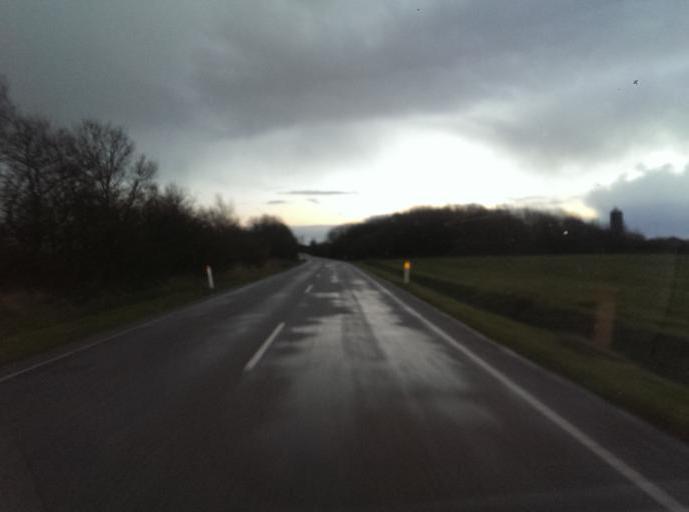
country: DK
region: South Denmark
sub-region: Esbjerg Kommune
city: Bramming
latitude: 55.4520
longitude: 8.6882
